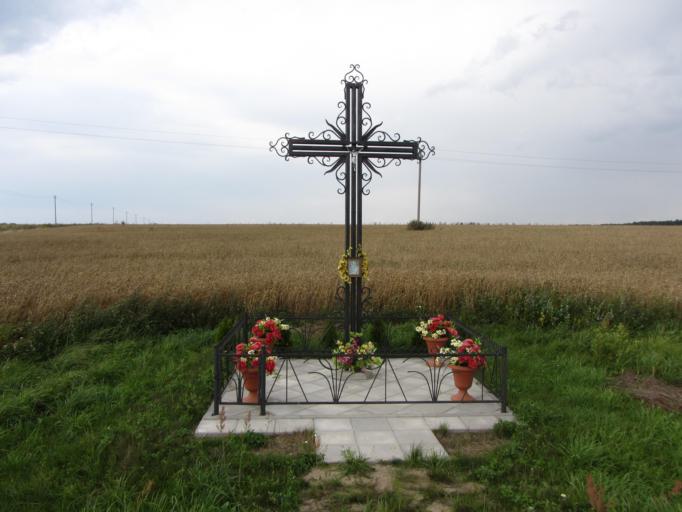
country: LT
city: Salcininkai
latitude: 54.3523
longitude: 25.4663
